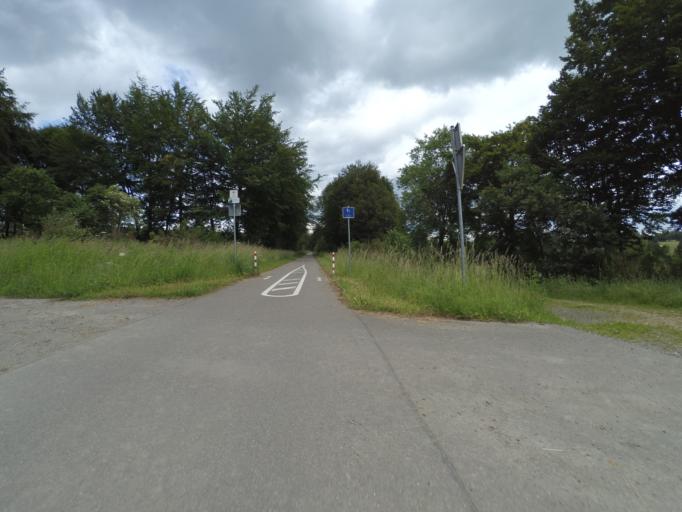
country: DE
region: North Rhine-Westphalia
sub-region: Regierungsbezirk Koln
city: Monschau
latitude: 50.5788
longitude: 6.2394
